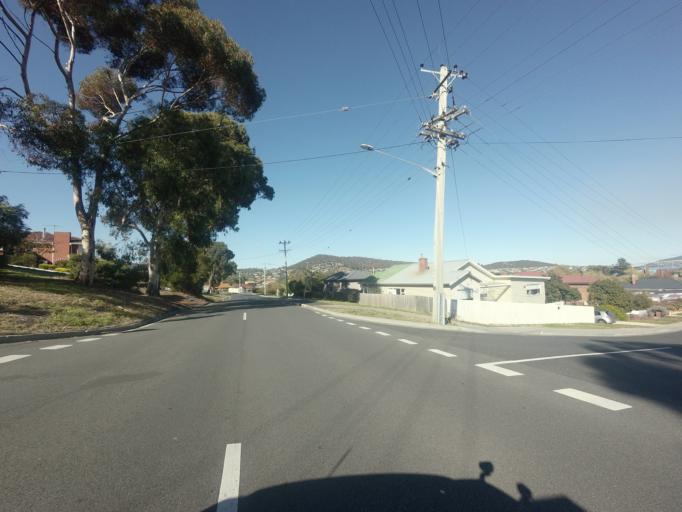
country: AU
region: Tasmania
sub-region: Clarence
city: Lindisfarne
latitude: -42.8481
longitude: 147.3467
